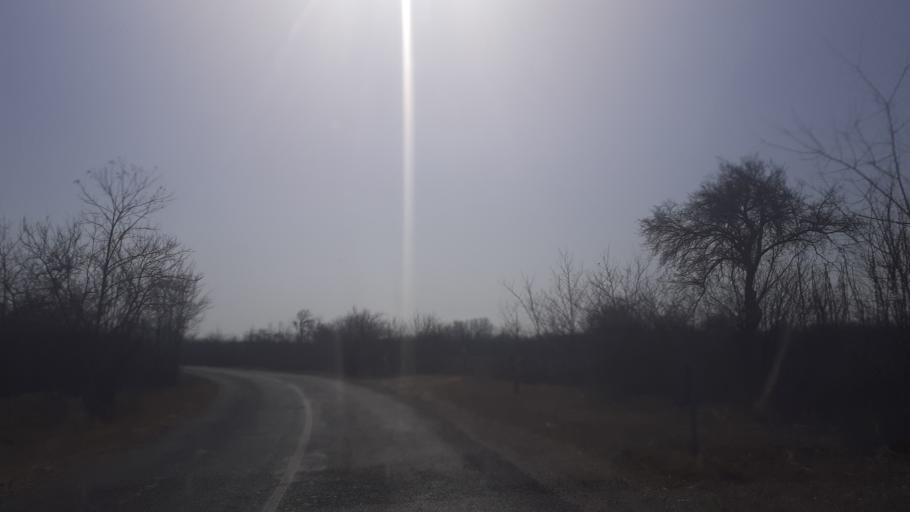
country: HU
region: Pest
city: Dabas
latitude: 47.1418
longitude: 19.3277
